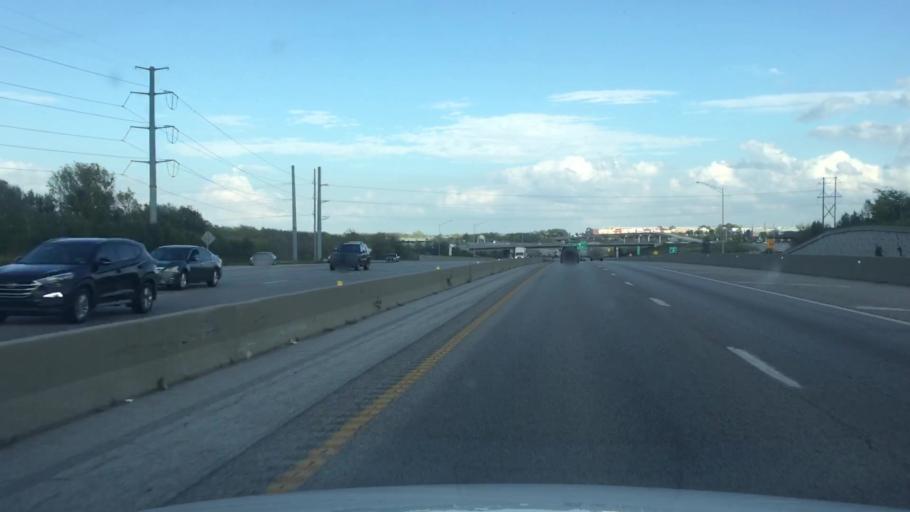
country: US
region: Missouri
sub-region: Jackson County
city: Lees Summit
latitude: 38.9342
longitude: -94.4189
